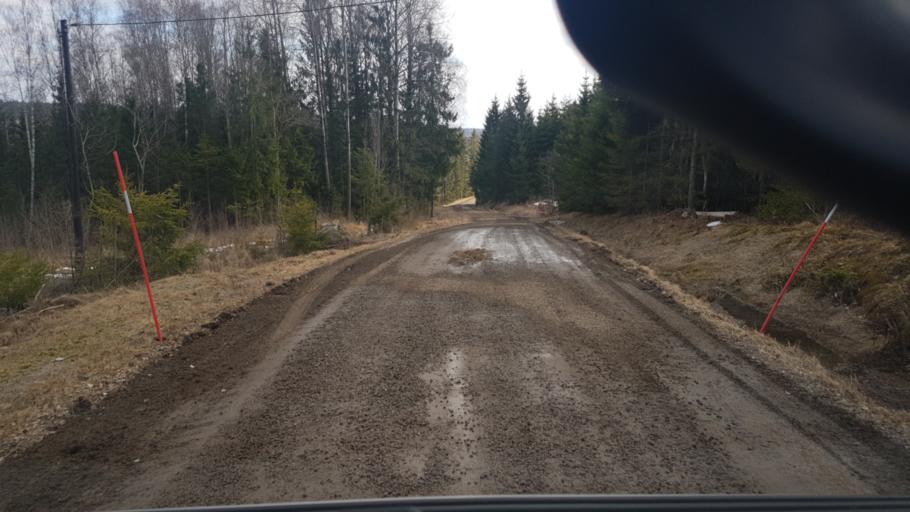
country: SE
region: Vaermland
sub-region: Eda Kommun
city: Amotfors
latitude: 59.7922
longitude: 12.4269
